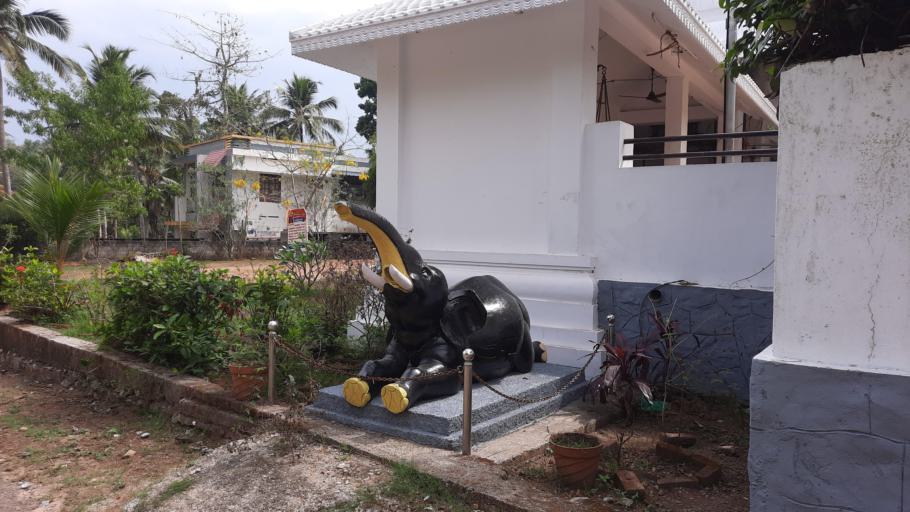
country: IN
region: Kerala
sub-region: Thiruvananthapuram
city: Thiruvananthapuram
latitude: 8.5573
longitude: 76.9302
